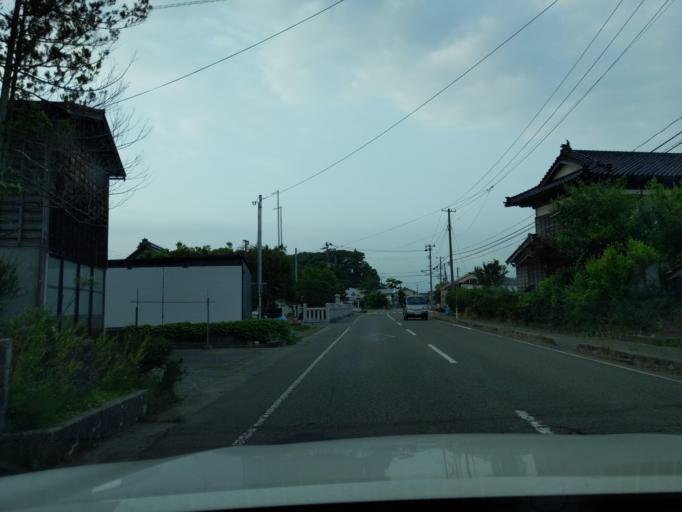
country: JP
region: Niigata
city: Kashiwazaki
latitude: 37.4197
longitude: 138.6158
